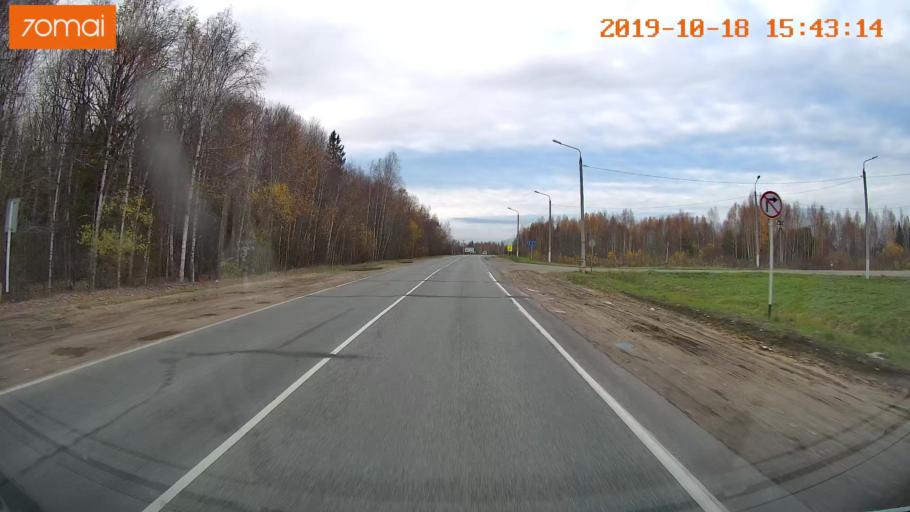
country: RU
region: Vladimir
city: Golovino
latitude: 55.9650
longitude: 40.5537
